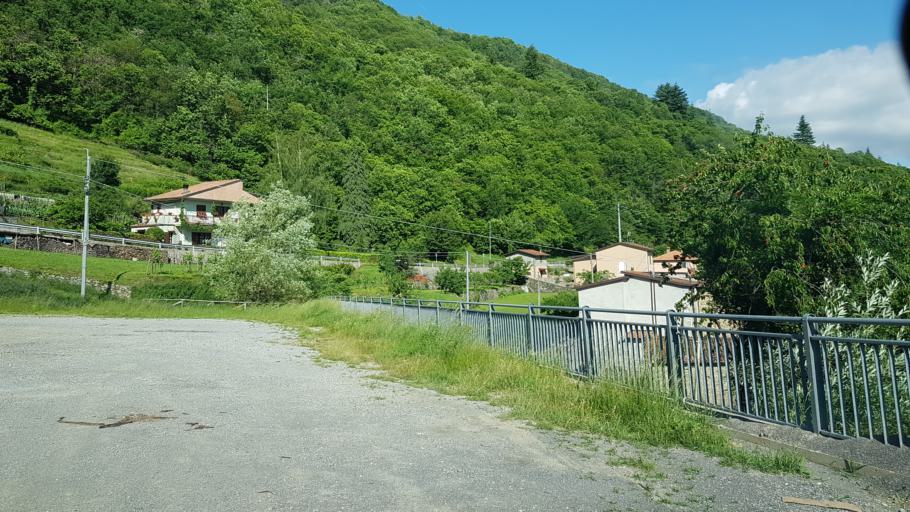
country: IT
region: Tuscany
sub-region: Provincia di Lucca
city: San Romano
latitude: 44.1799
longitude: 10.3357
